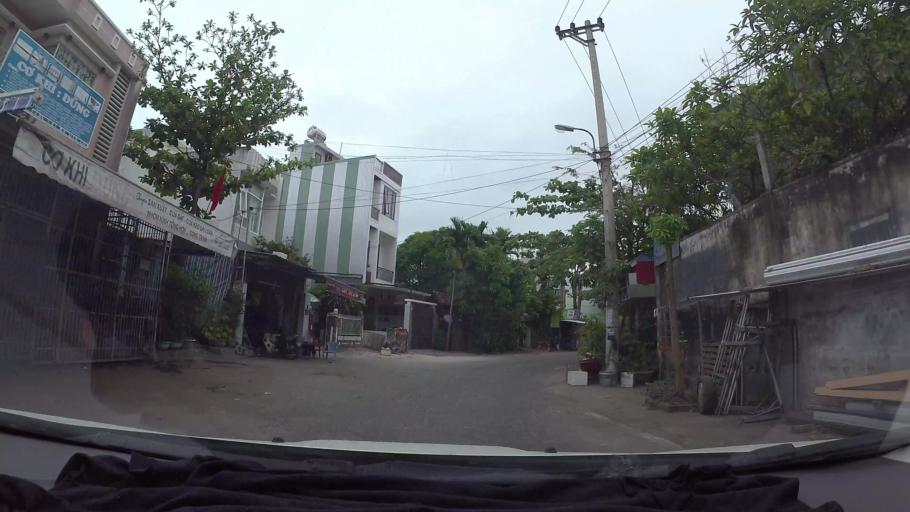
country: VN
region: Da Nang
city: Thanh Khe
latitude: 16.0686
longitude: 108.1776
